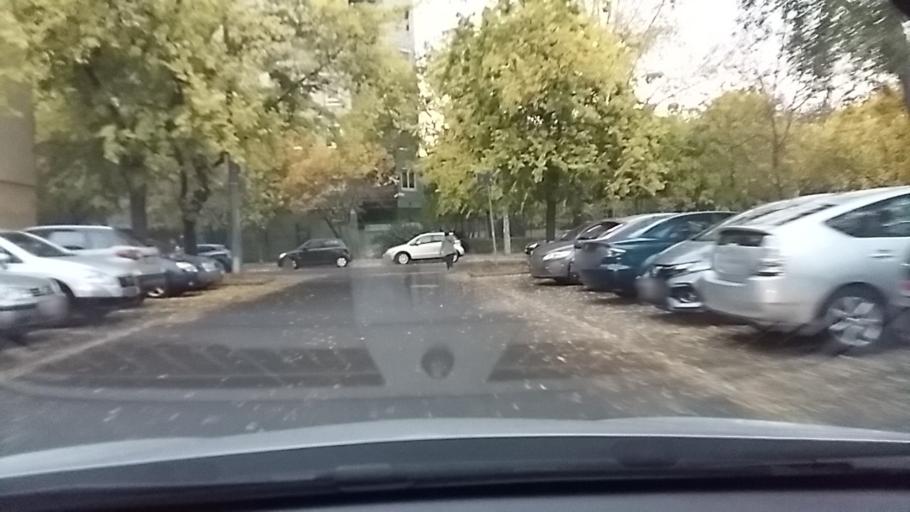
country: HU
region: Budapest
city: Budapest XV. keruelet
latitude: 47.5886
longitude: 19.1153
